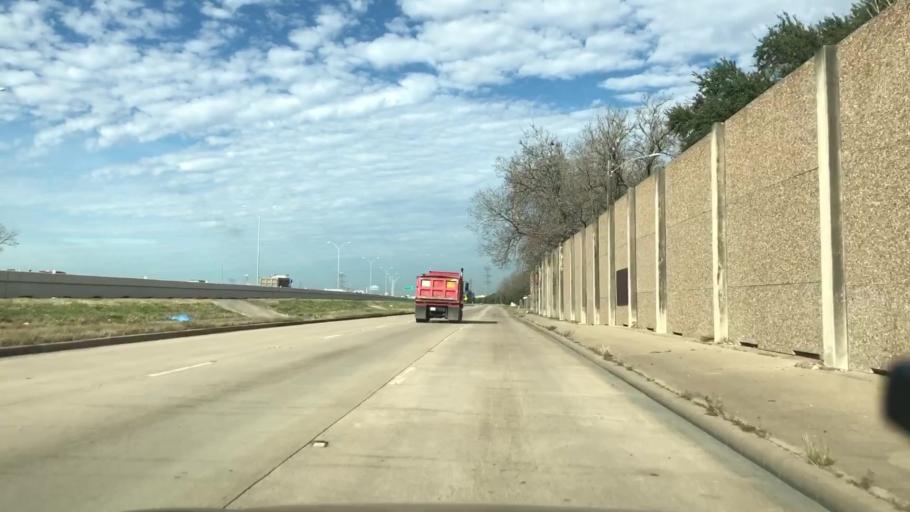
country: US
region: Texas
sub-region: Fort Bend County
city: Missouri City
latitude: 29.6172
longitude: -95.4999
